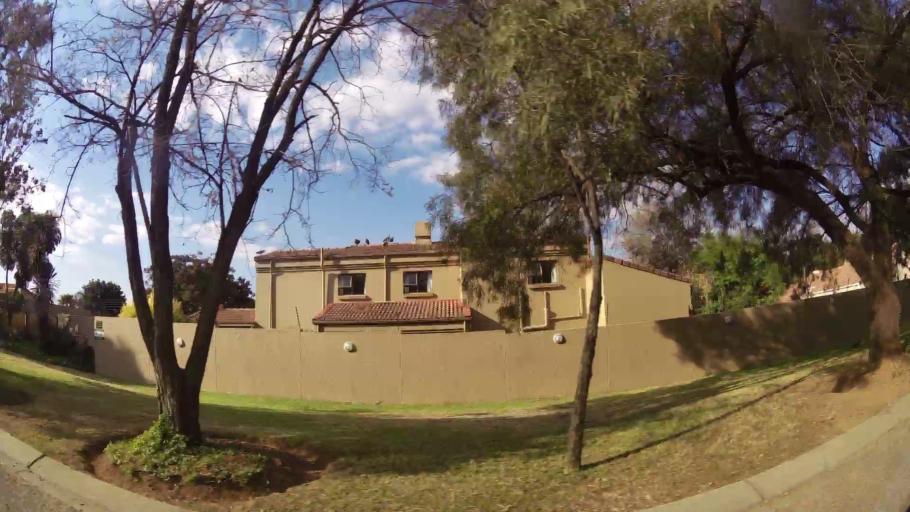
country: ZA
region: Gauteng
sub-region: City of Johannesburg Metropolitan Municipality
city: Diepsloot
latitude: -26.0039
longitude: 28.0271
